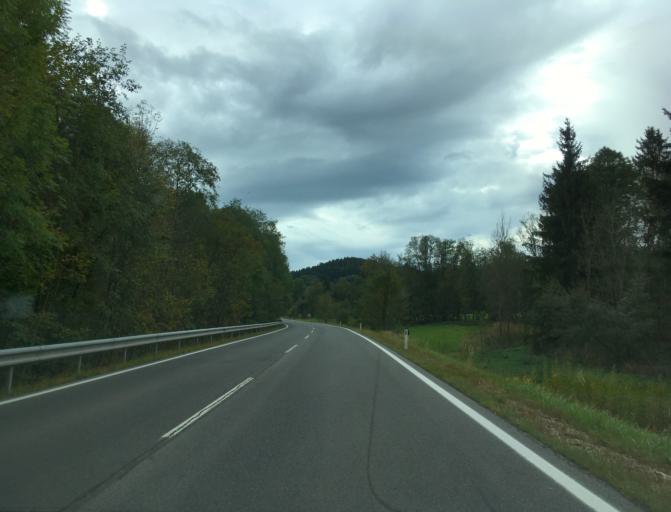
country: AT
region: Lower Austria
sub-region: Politischer Bezirk Neunkirchen
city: Thomasberg
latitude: 47.5521
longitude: 16.1431
